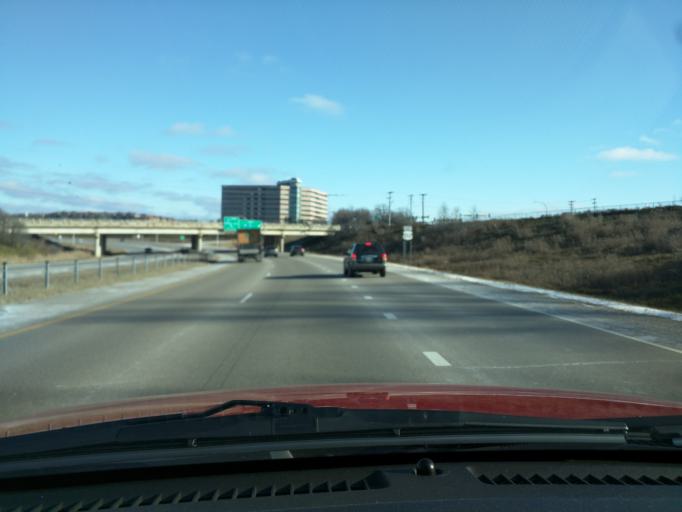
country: US
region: Minnesota
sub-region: Hennepin County
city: Eden Prairie
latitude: 44.8659
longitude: -93.4218
